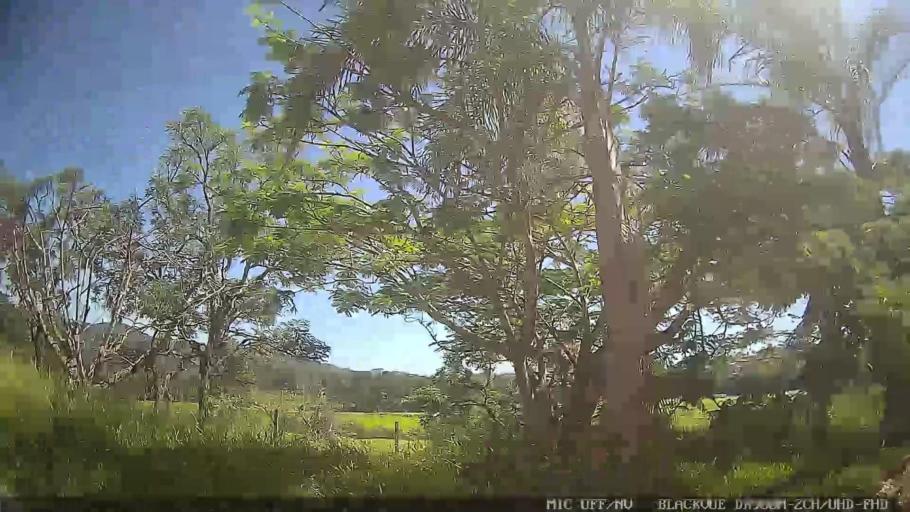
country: BR
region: Sao Paulo
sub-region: Atibaia
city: Atibaia
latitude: -23.1013
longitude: -46.5740
